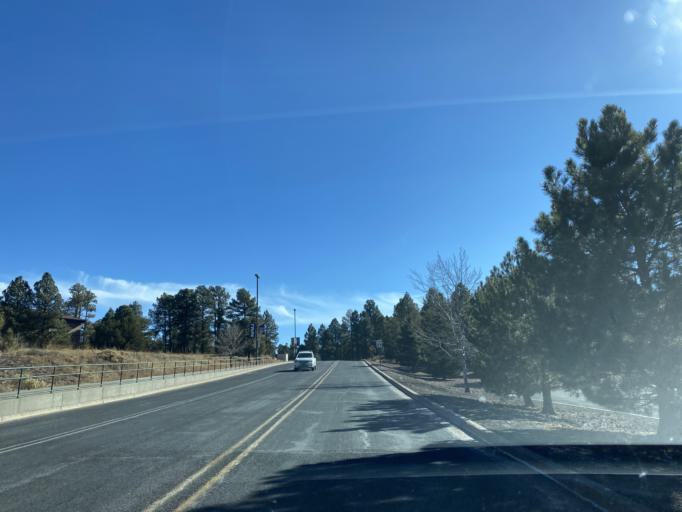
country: US
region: Arizona
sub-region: Coconino County
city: Flagstaff
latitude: 35.1765
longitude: -111.6592
